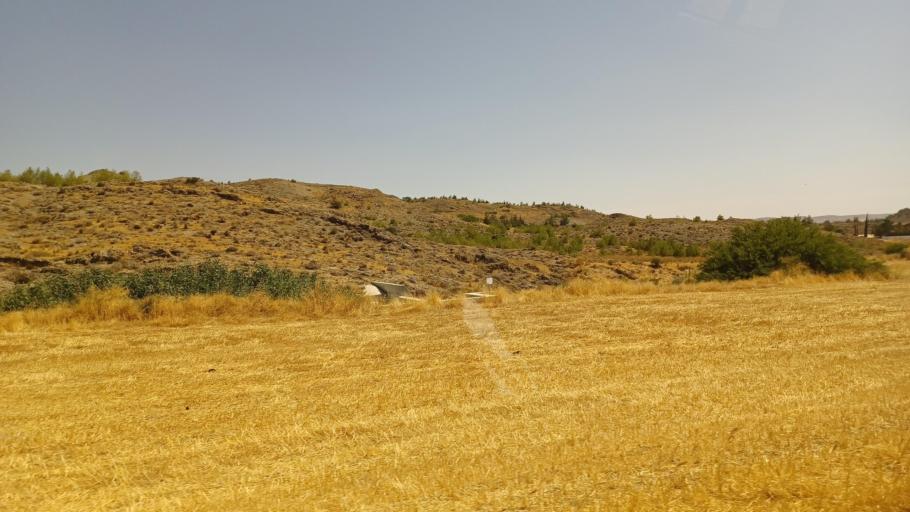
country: CY
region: Larnaka
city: Aradippou
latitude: 35.0027
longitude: 33.5625
